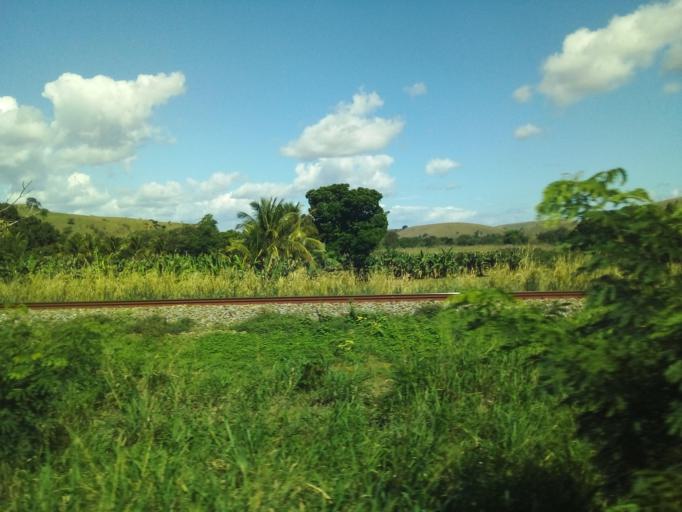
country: BR
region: Minas Gerais
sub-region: Governador Valadares
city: Governador Valadares
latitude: -18.8552
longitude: -41.8623
